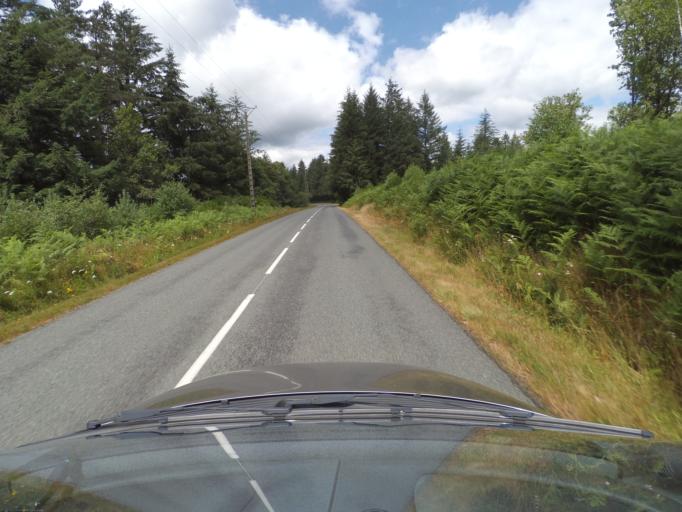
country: FR
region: Limousin
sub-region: Departement de la Haute-Vienne
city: Peyrat-le-Chateau
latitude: 45.8778
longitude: 1.8974
